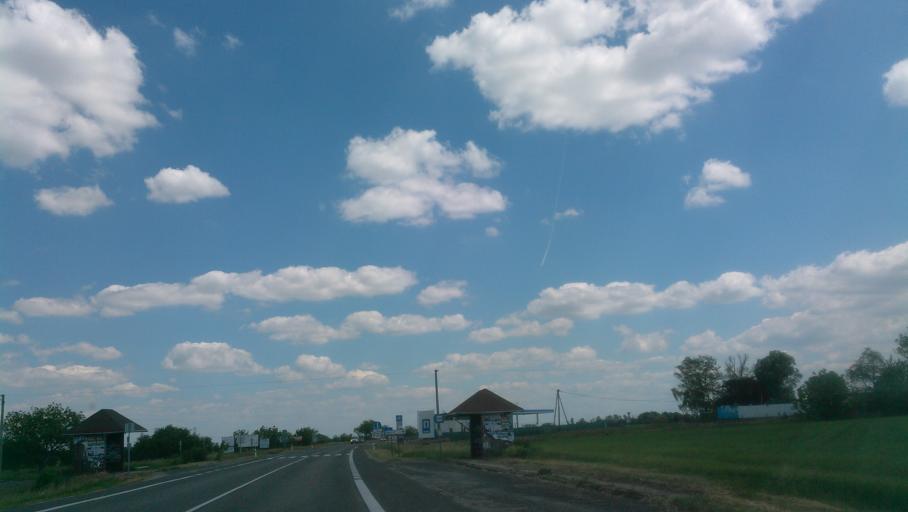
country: SK
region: Trnavsky
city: Dunajska Streda
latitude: 48.0009
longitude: 17.4863
